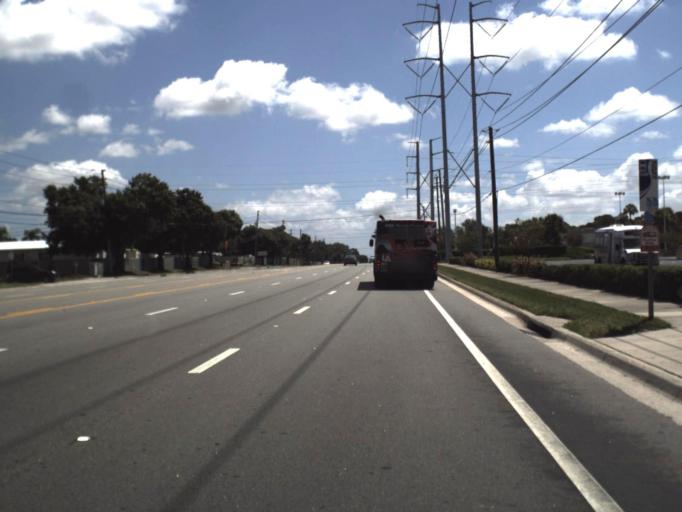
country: US
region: Florida
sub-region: Pinellas County
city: Saint George
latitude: 28.0193
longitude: -82.7328
